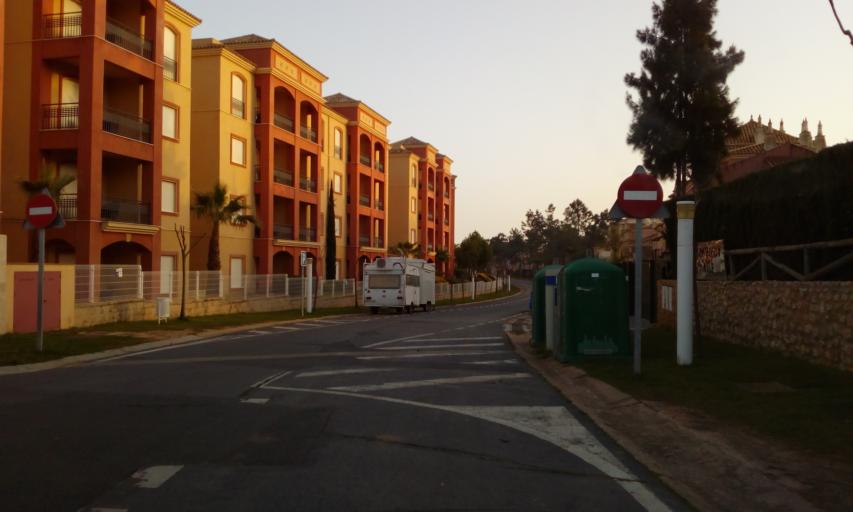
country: ES
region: Andalusia
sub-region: Provincia de Huelva
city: Lepe
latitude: 37.2151
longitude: -7.2271
